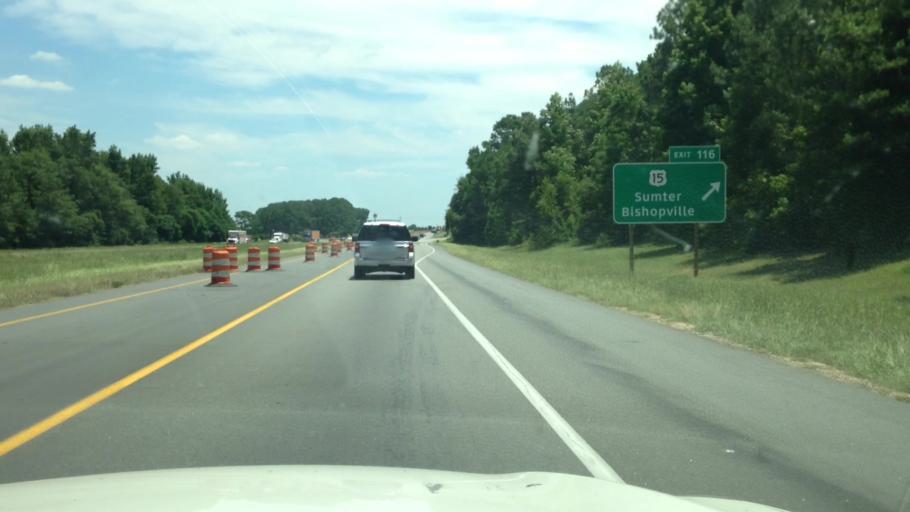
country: US
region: South Carolina
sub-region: Lee County
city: Bishopville
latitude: 34.1954
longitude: -80.2893
